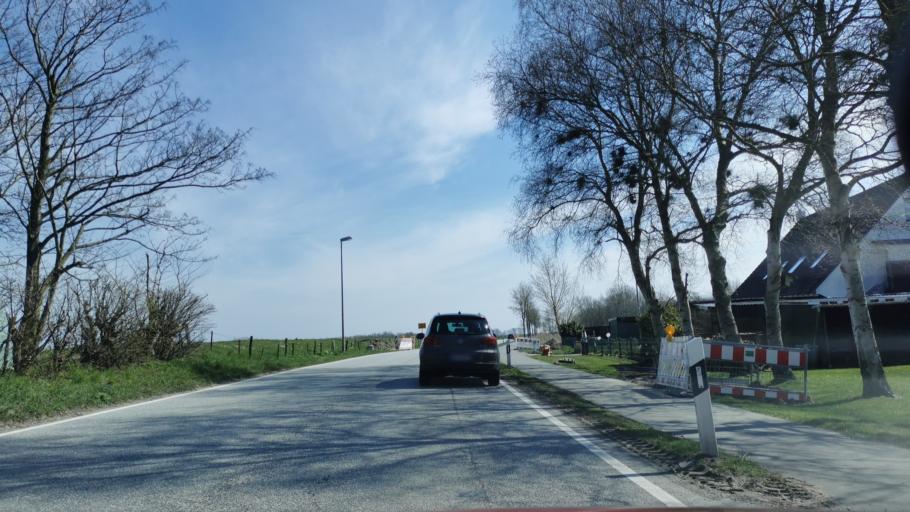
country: DE
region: Schleswig-Holstein
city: Oesterdeichstrich
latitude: 54.1577
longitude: 8.9073
